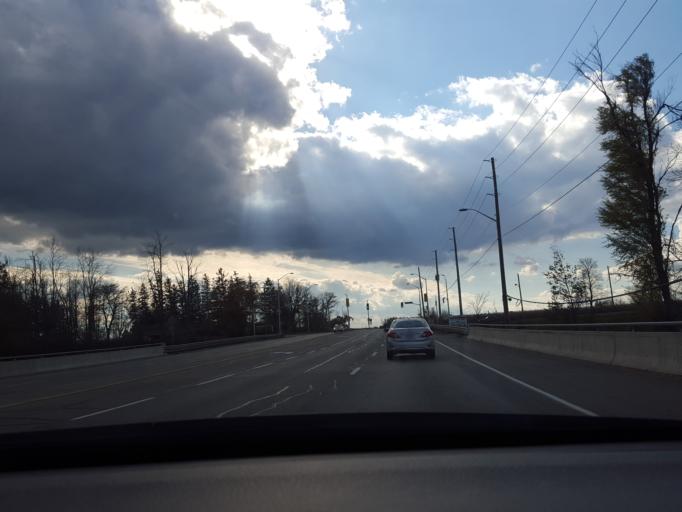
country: CA
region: Ontario
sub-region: Halton
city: Milton
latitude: 43.5460
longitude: -79.8186
